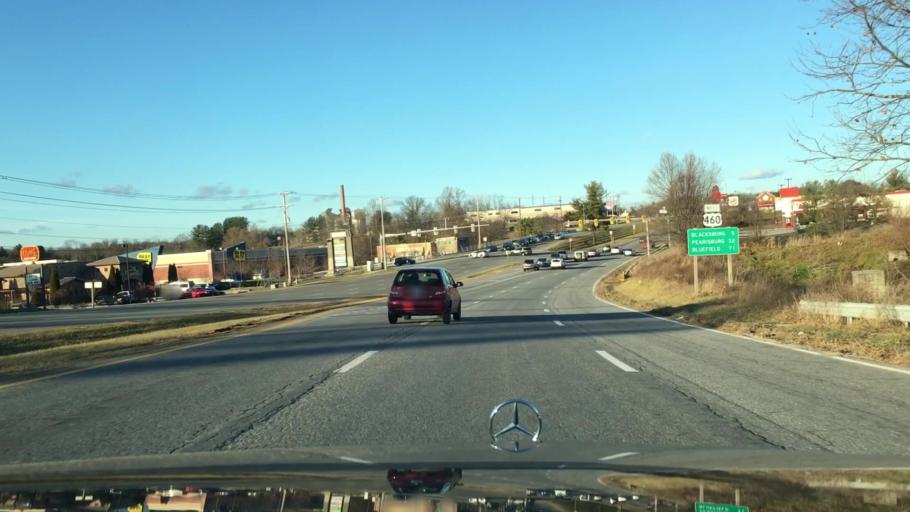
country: US
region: Virginia
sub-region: Montgomery County
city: Merrimac
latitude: 37.1646
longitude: -80.4233
